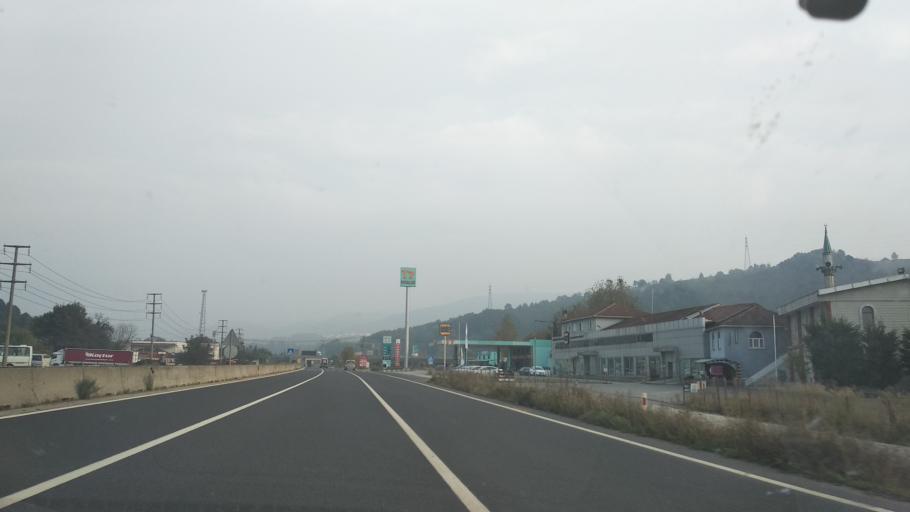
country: TR
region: Duzce
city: Kaynasli
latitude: 40.7886
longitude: 31.2604
